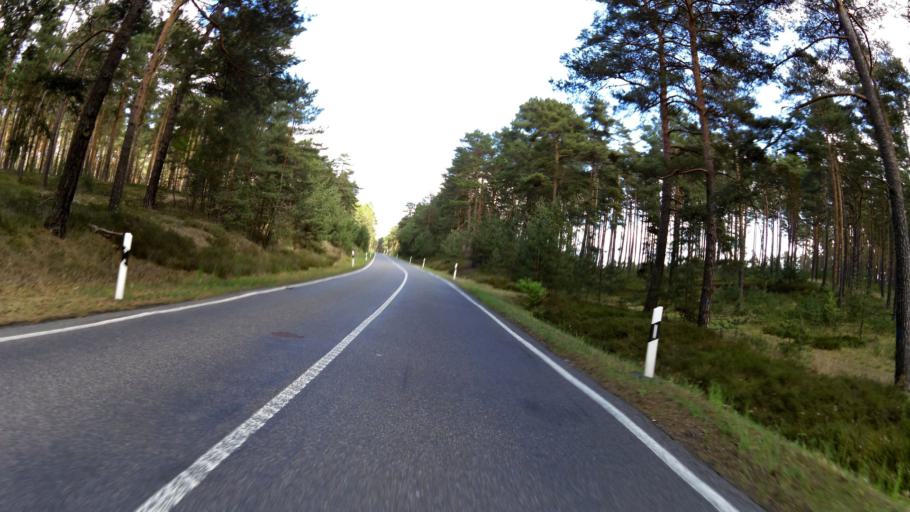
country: DE
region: Brandenburg
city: Wendisch Rietz
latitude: 52.1345
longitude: 13.9627
